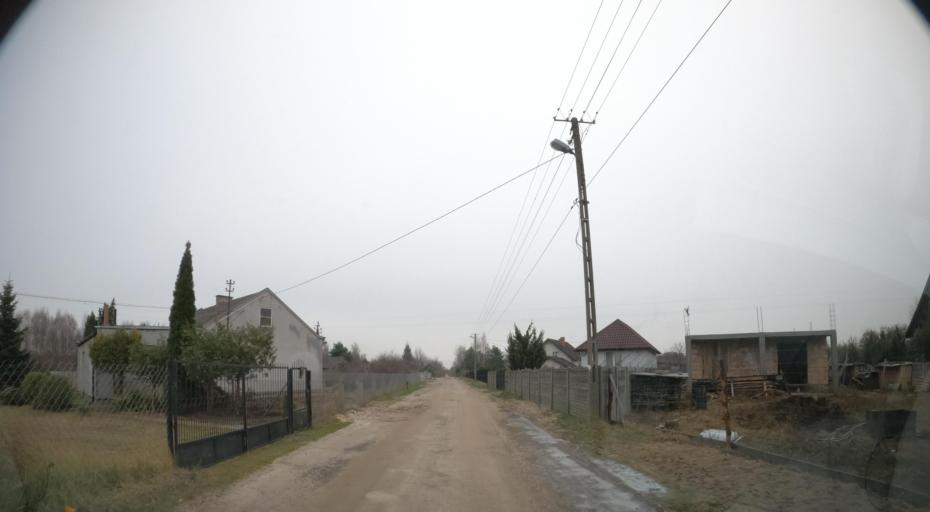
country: PL
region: Masovian Voivodeship
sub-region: Powiat radomski
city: Jastrzebia
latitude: 51.4883
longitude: 21.1880
